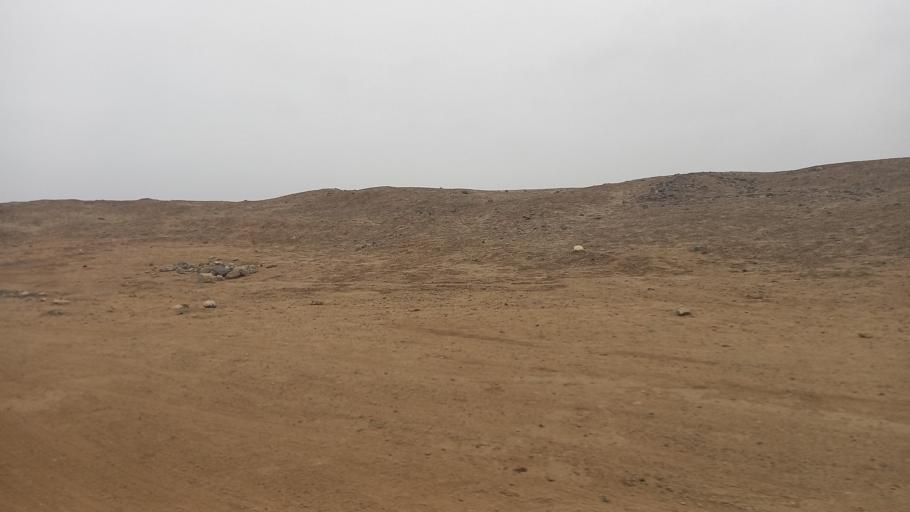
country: PE
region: La Libertad
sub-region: Provincia de Trujillo
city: Huanchaco
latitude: -8.1018
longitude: -79.0790
